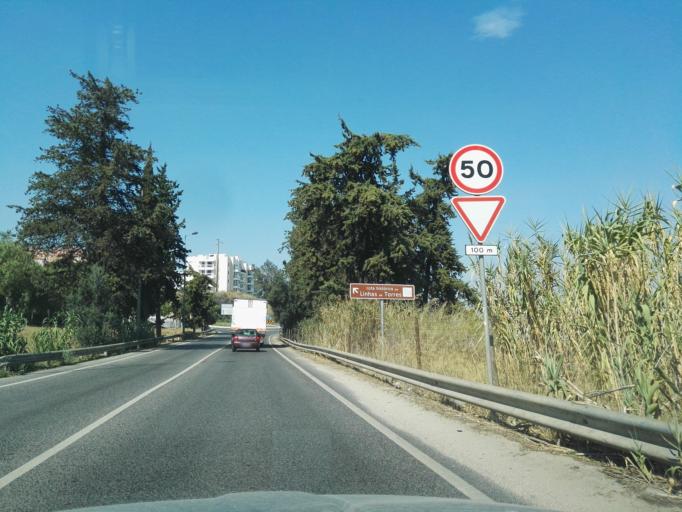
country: PT
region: Lisbon
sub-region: Vila Franca de Xira
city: Vialonga
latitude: 38.8752
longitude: -9.0528
